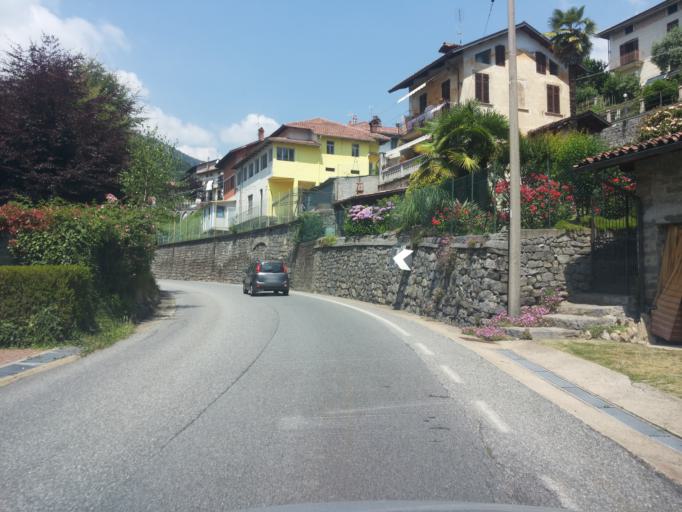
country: IT
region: Piedmont
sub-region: Provincia di Biella
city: Sagliano Micca
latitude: 45.6325
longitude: 8.0385
